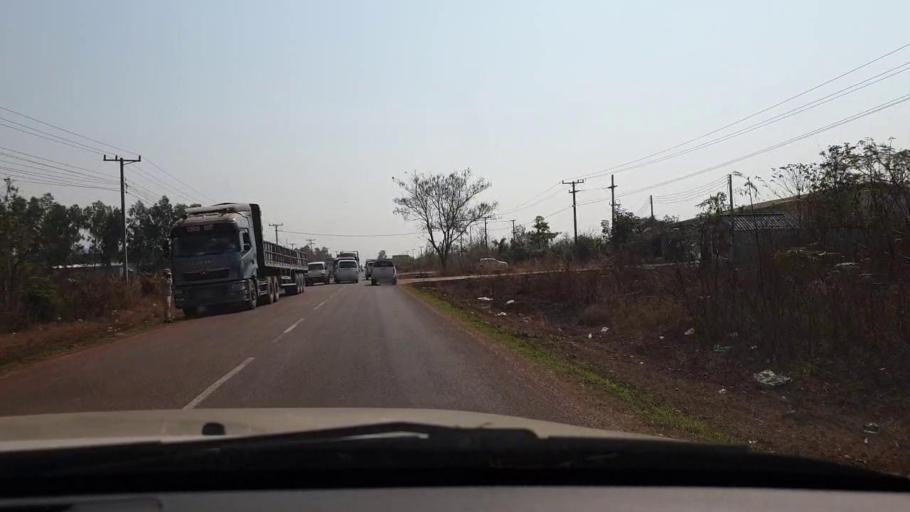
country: TH
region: Nong Khai
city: Nong Khai
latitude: 18.0534
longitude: 102.8423
